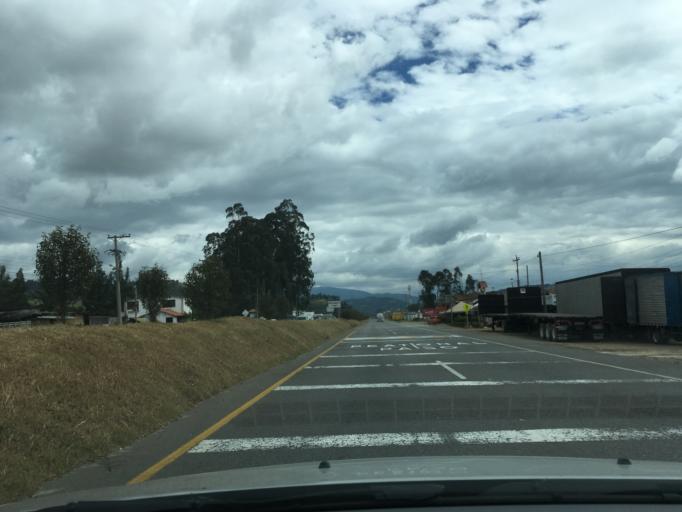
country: CO
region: Boyaca
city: Paipa
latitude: 5.7887
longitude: -73.0727
